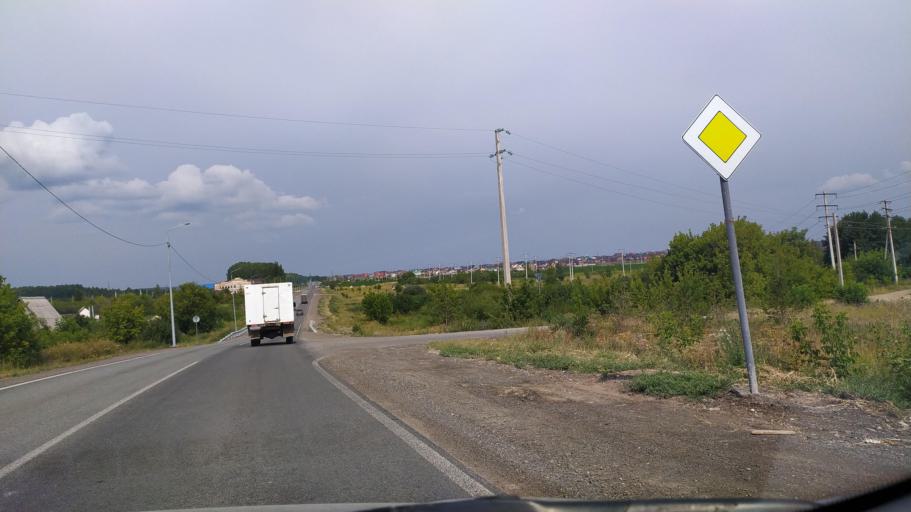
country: RU
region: Tatarstan
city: Al'met'yevsk
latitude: 54.8850
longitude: 52.2524
